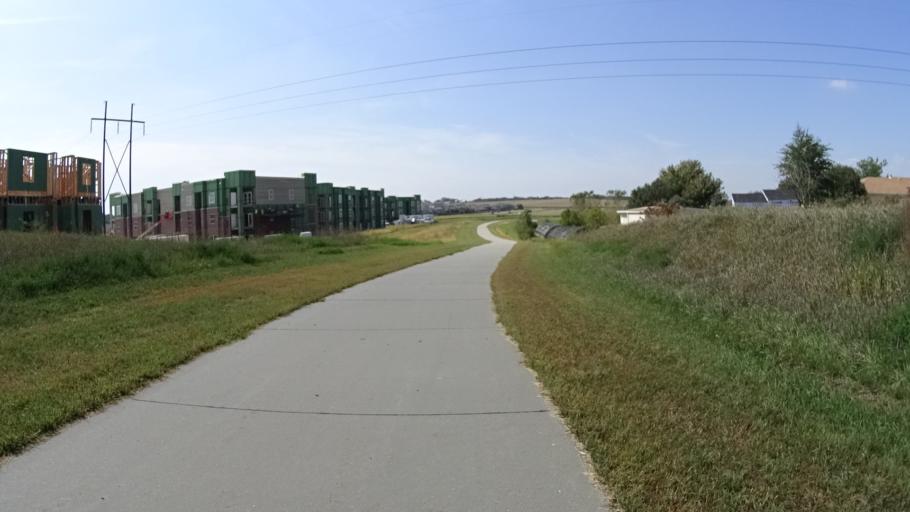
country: US
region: Nebraska
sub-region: Sarpy County
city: Offutt Air Force Base
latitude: 41.1480
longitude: -95.9759
